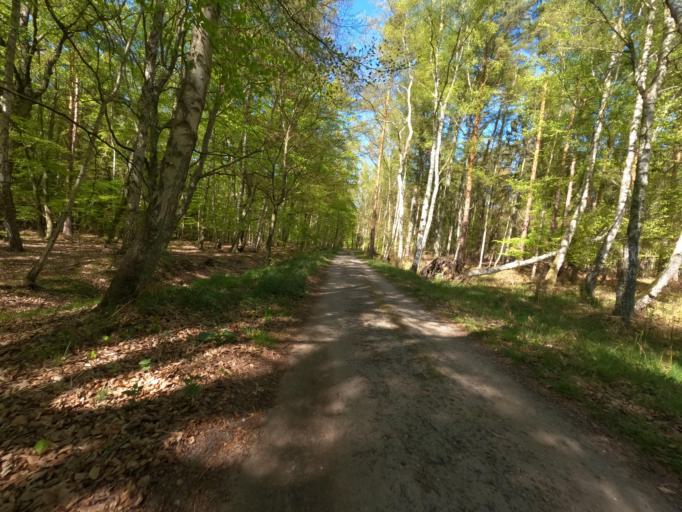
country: DE
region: Mecklenburg-Vorpommern
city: Born
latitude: 54.4245
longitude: 12.5363
